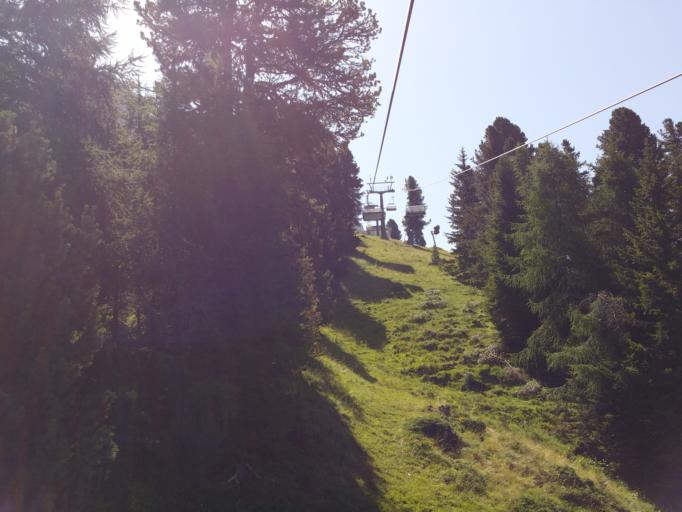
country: IT
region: Trentino-Alto Adige
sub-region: Bolzano
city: Nova Levante
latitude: 46.3735
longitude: 11.5406
